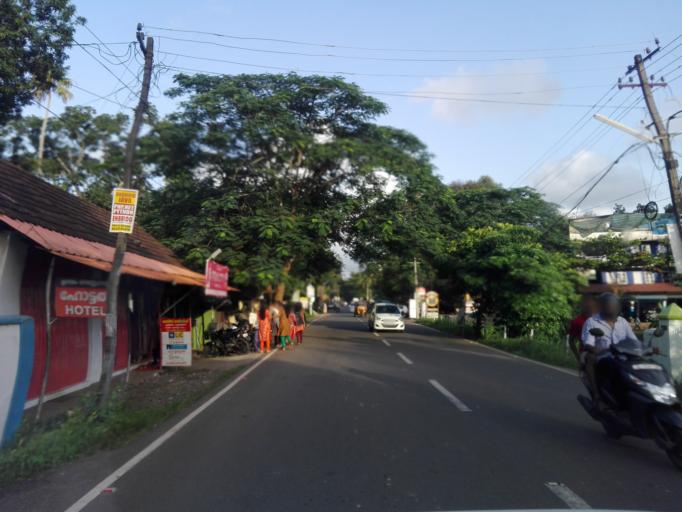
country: IN
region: Kerala
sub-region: Kottayam
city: Kottayam
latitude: 9.6074
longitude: 76.5120
